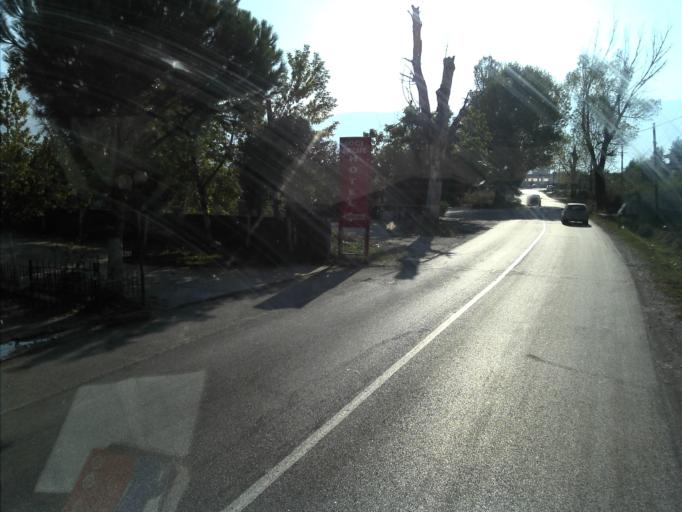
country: AL
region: Gjirokaster
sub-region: Rrethi i Gjirokastres
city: Lazarat
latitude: 40.0646
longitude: 20.1675
